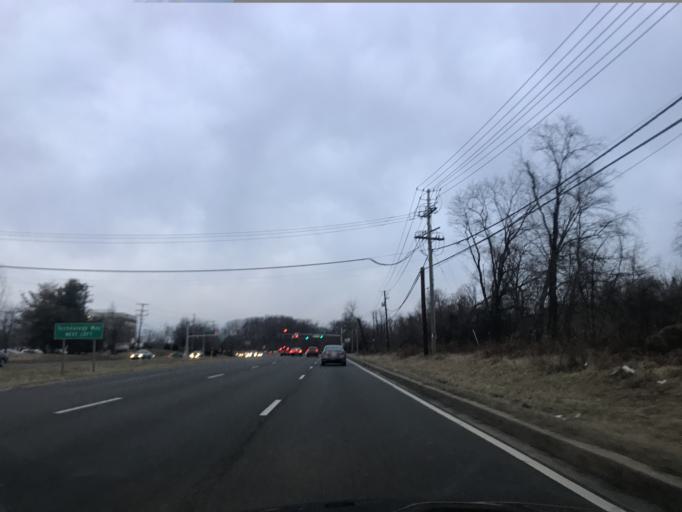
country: US
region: Maryland
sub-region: Prince George's County
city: Lake Arbor
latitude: 38.9066
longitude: -76.8342
